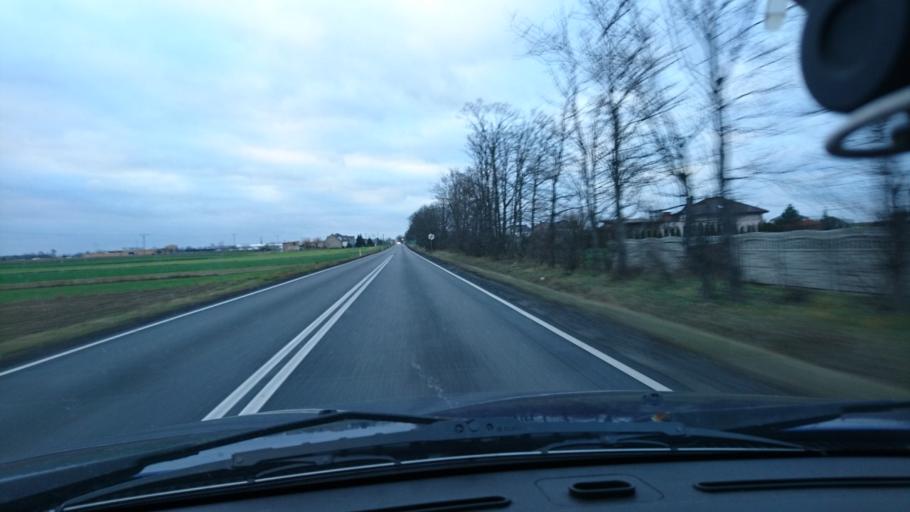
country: PL
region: Greater Poland Voivodeship
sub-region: Powiat kepinski
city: Slupia pod Kepnem
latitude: 51.2354
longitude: 18.0545
